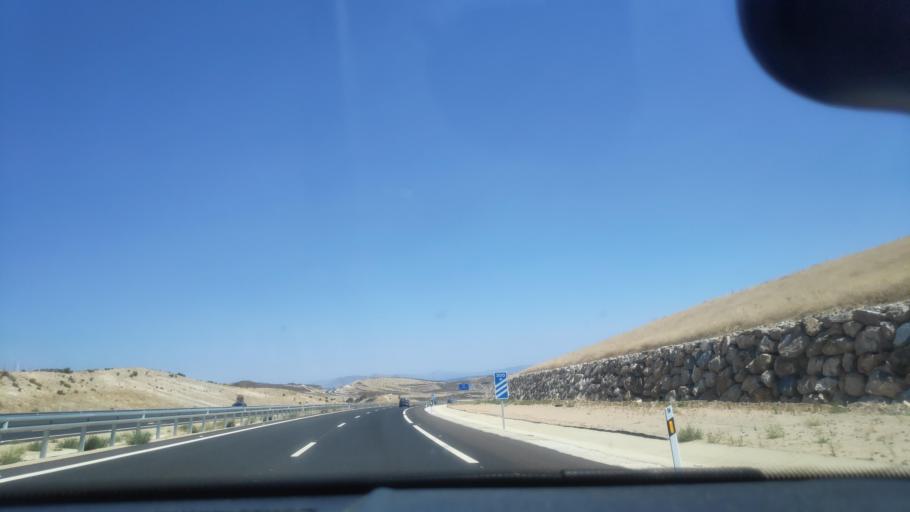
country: ES
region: Andalusia
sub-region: Provincia de Granada
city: Alhendin
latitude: 37.0945
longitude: -3.6735
